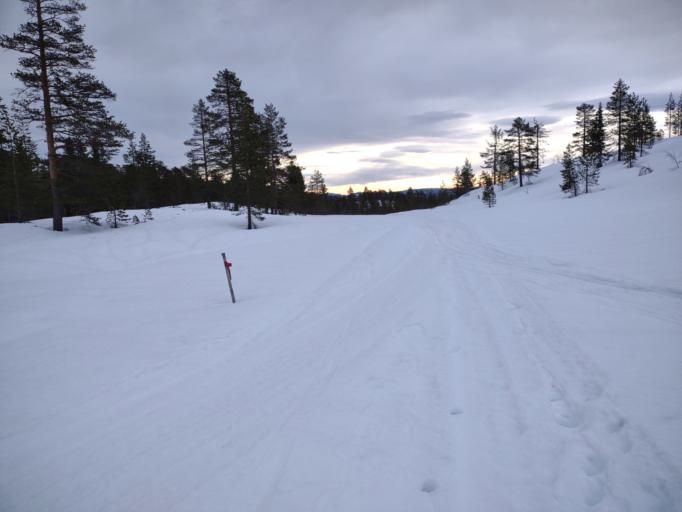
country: NO
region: Buskerud
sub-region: Flesberg
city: Lampeland
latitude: 59.7513
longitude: 9.4701
